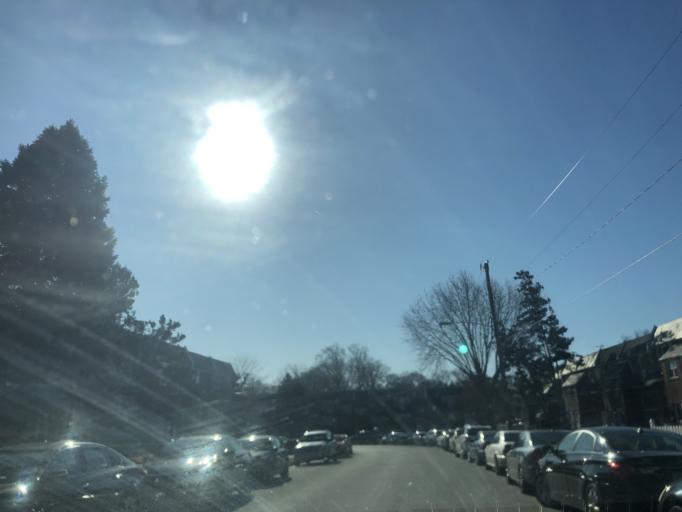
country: US
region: Pennsylvania
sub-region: Montgomery County
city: Bala-Cynwyd
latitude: 40.0004
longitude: -75.2131
